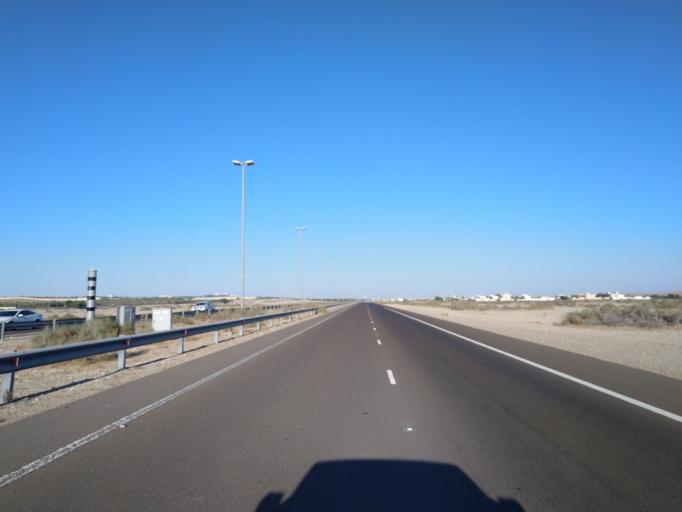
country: OM
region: Al Buraimi
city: Al Buraymi
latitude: 24.5059
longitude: 55.4622
